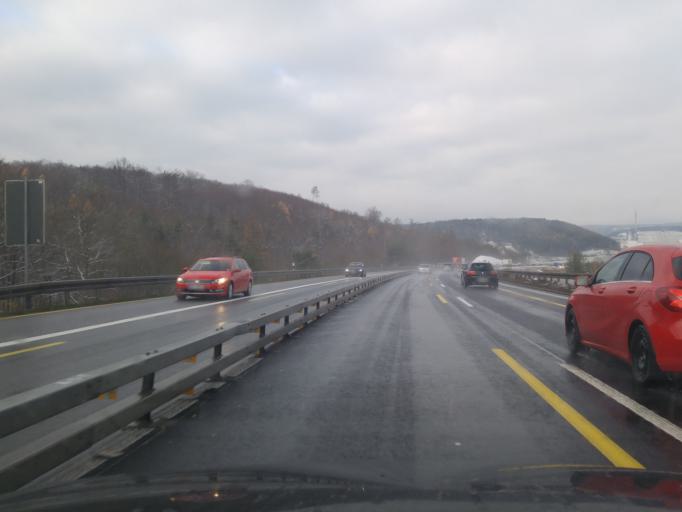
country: DE
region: Bavaria
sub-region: Regierungsbezirk Unterfranken
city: Fuchsstadt
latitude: 50.1057
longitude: 9.9646
